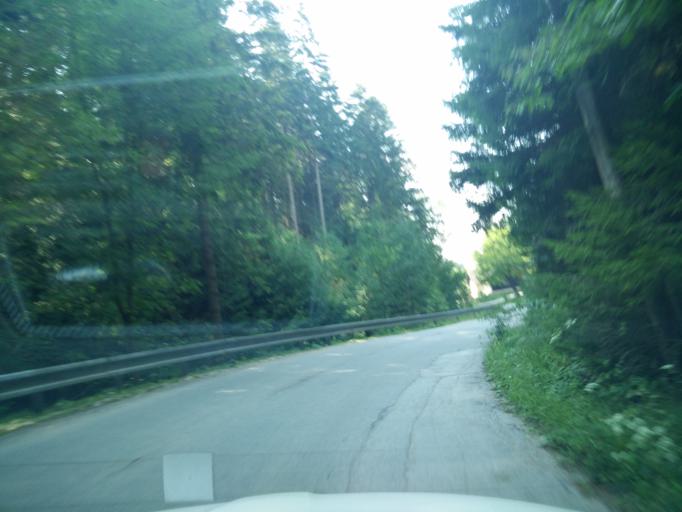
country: SK
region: Zilinsky
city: Rajec
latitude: 49.0923
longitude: 18.7191
